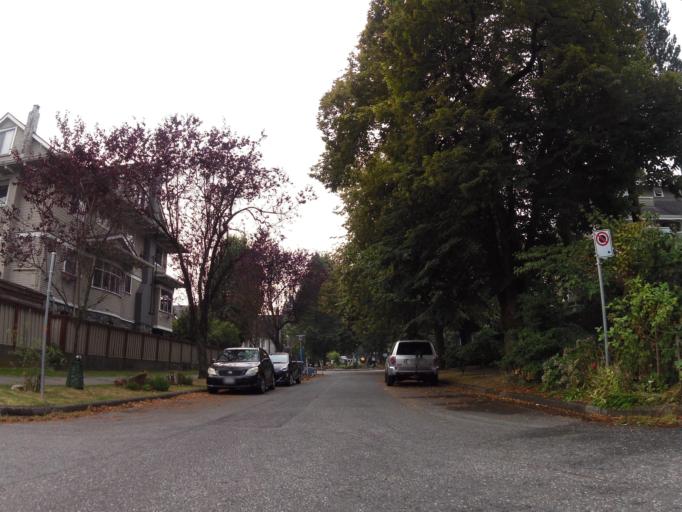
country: CA
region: British Columbia
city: West End
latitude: 49.2595
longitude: -123.1483
